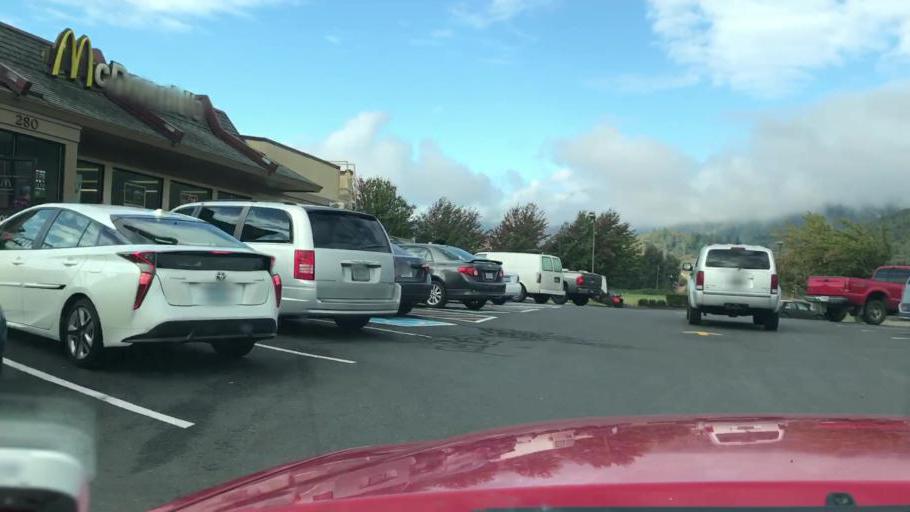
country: US
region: Oregon
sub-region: Douglas County
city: Tri-City
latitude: 42.9733
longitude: -123.3403
